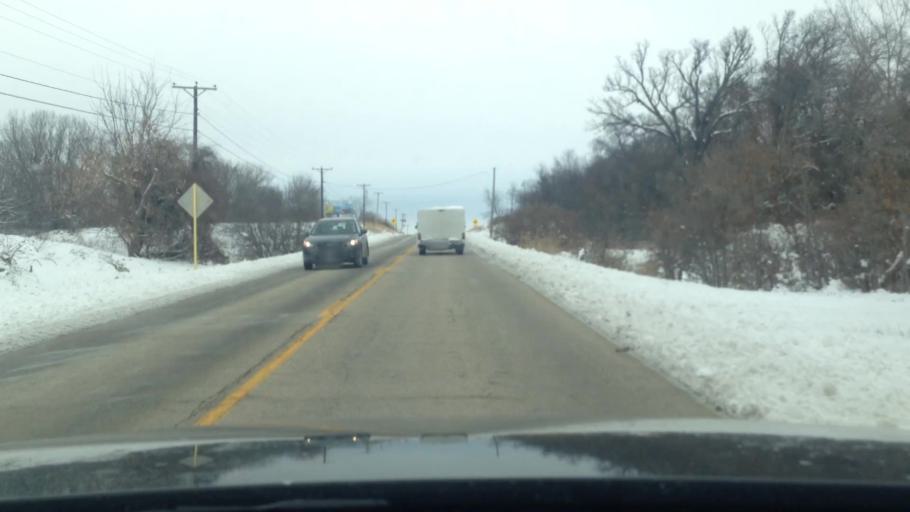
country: US
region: Illinois
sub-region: McHenry County
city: Hebron
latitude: 42.4902
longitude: -88.4424
